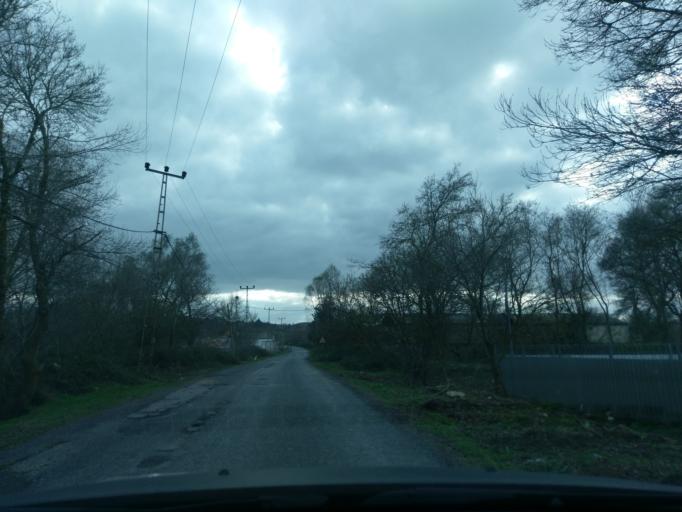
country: TR
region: Istanbul
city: Durusu
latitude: 41.2966
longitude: 28.6769
